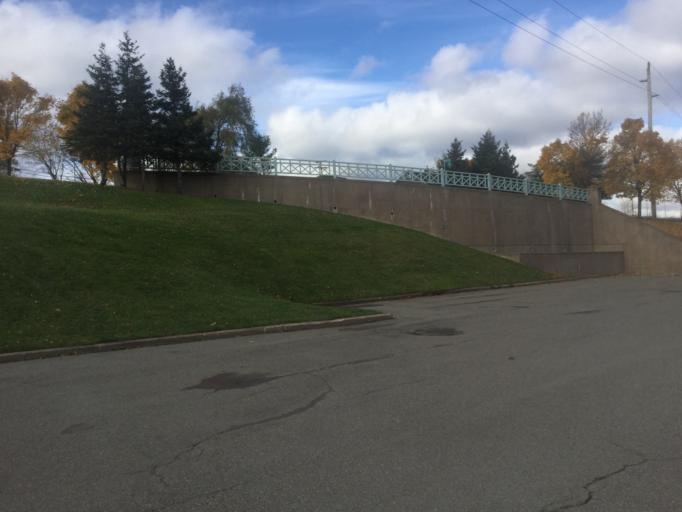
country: CA
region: Nova Scotia
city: New Glasgow
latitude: 45.5677
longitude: -62.6584
